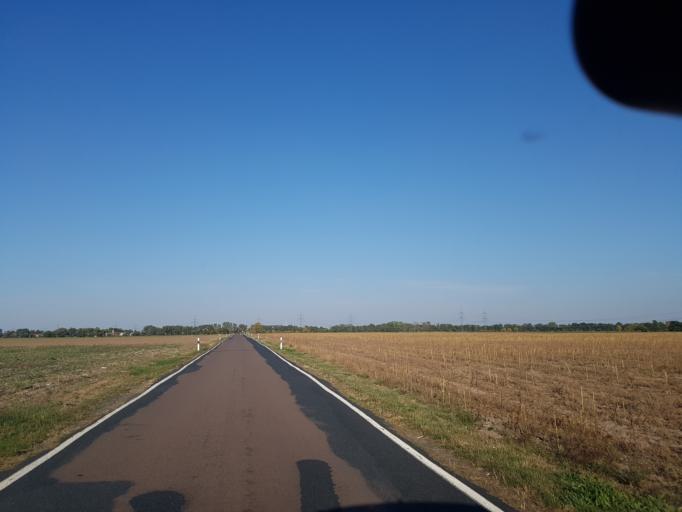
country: DE
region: Saxony
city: Nauwalde
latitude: 51.4085
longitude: 13.3780
